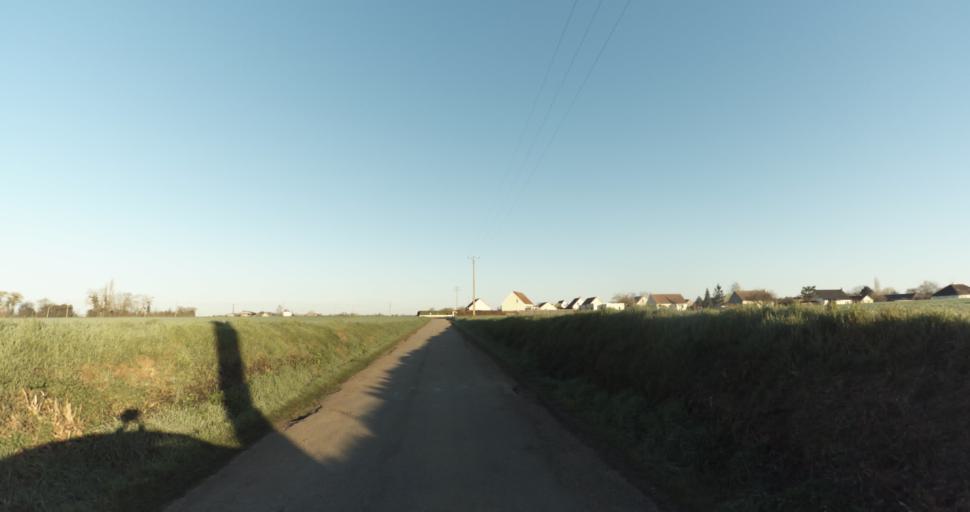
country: FR
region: Lower Normandy
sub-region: Departement du Calvados
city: Saint-Pierre-sur-Dives
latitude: 49.0312
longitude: -0.0278
